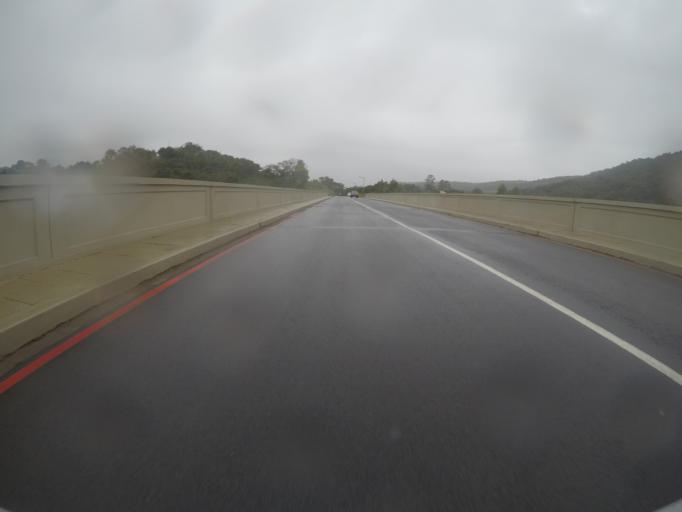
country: ZA
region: Eastern Cape
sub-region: Buffalo City Metropolitan Municipality
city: East London
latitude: -32.9532
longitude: 27.9052
